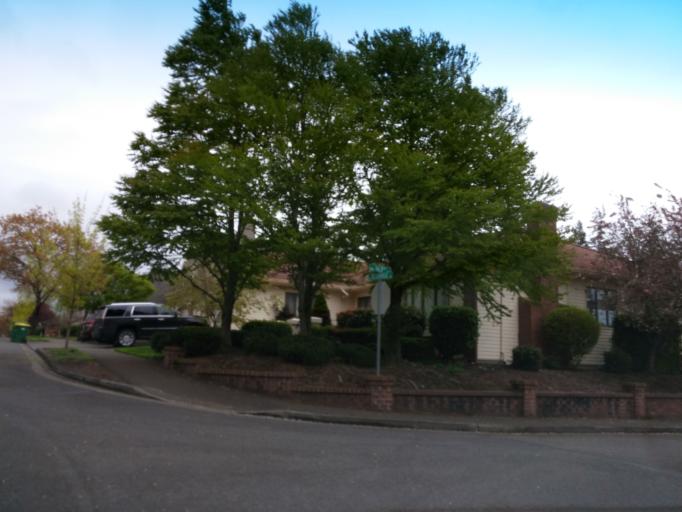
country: US
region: Oregon
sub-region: Washington County
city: Oak Hills
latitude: 45.5230
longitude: -122.8457
